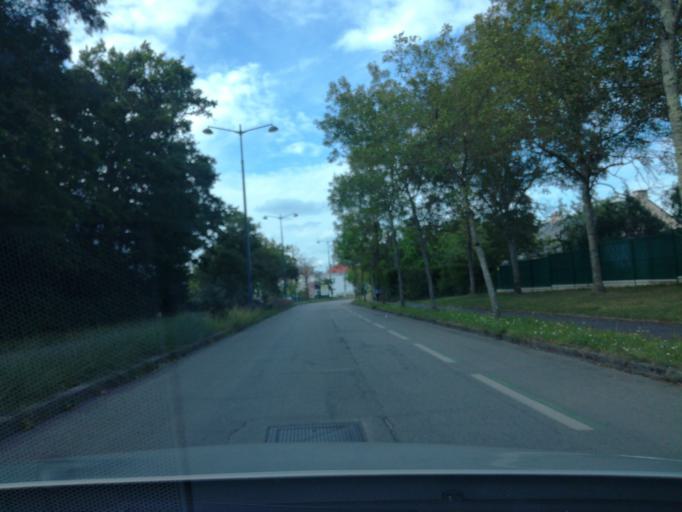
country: FR
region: Brittany
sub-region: Departement d'Ille-et-Vilaine
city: Saint-Gregoire
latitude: 48.1355
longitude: -1.6727
